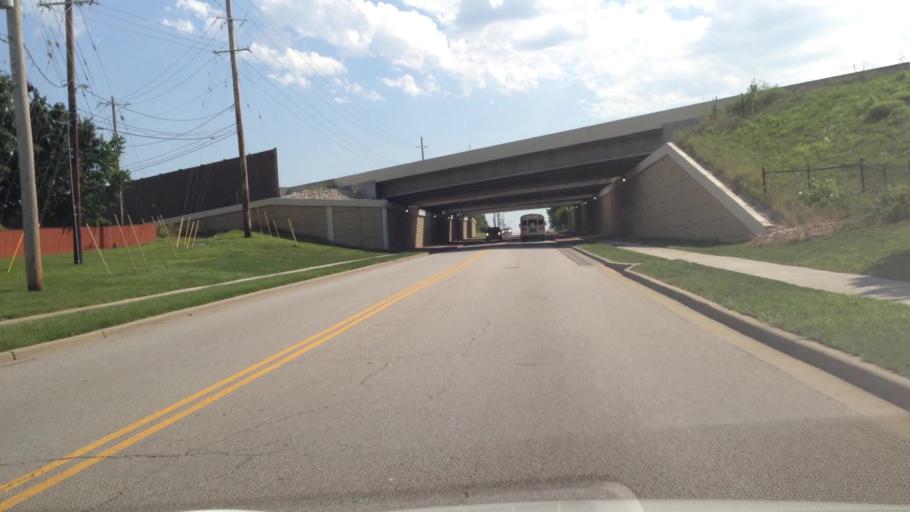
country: US
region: Kansas
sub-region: Johnson County
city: Lenexa
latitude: 38.9377
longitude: -94.7422
